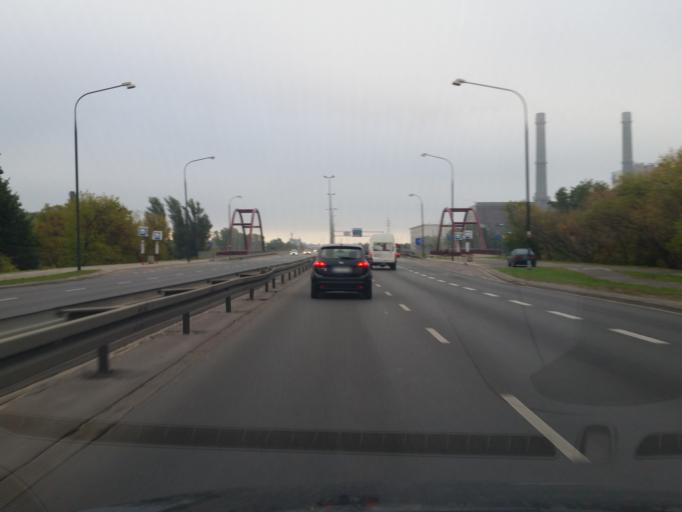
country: PL
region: Masovian Voivodeship
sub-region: Warszawa
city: Bialoleka
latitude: 52.3000
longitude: 20.9928
